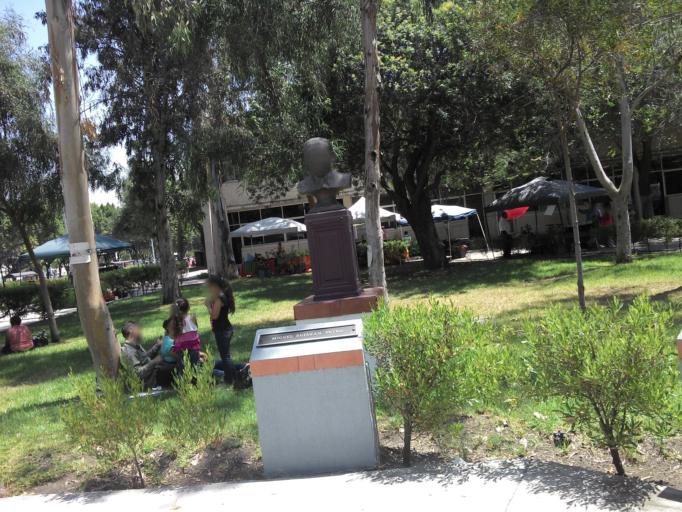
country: MX
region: Baja California
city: Tijuana
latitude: 32.5321
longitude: -117.0181
